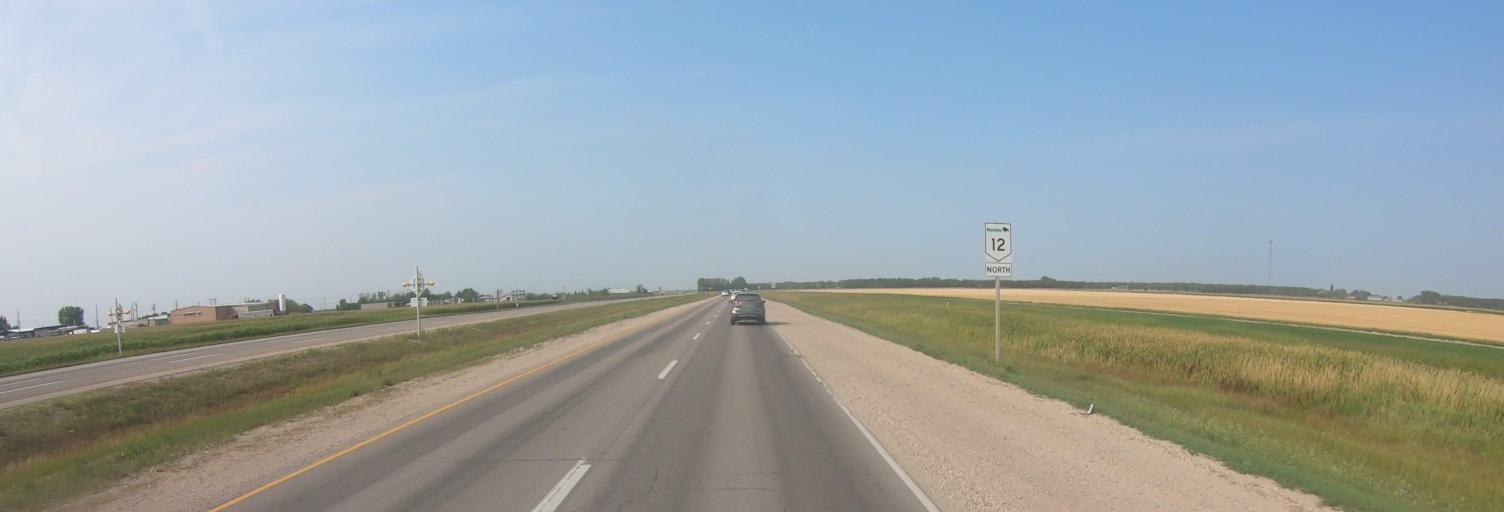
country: CA
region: Manitoba
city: Steinbach
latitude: 49.6054
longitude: -96.6822
